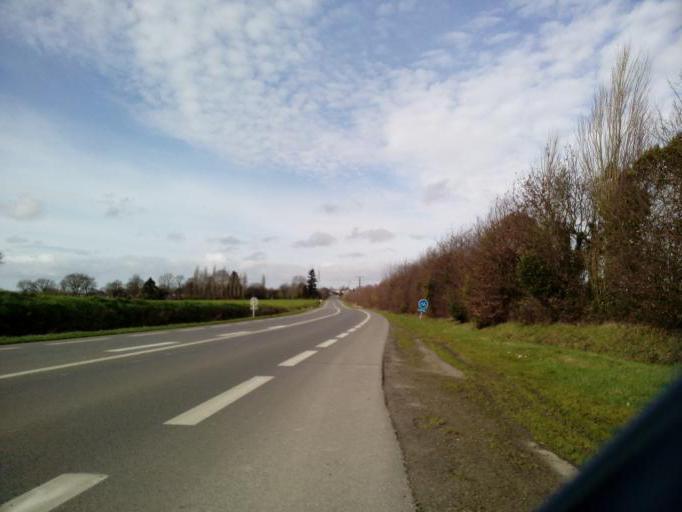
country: FR
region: Brittany
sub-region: Departement d'Ille-et-Vilaine
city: Montgermont
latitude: 48.1622
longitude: -1.7126
